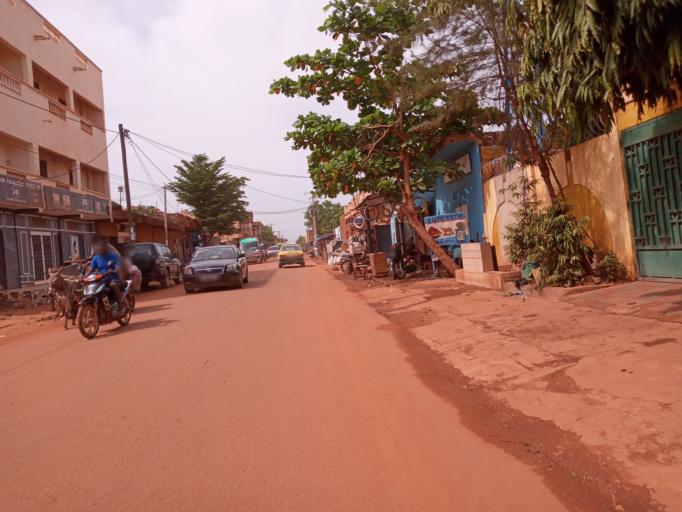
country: ML
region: Bamako
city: Bamako
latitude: 12.5567
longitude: -7.9904
